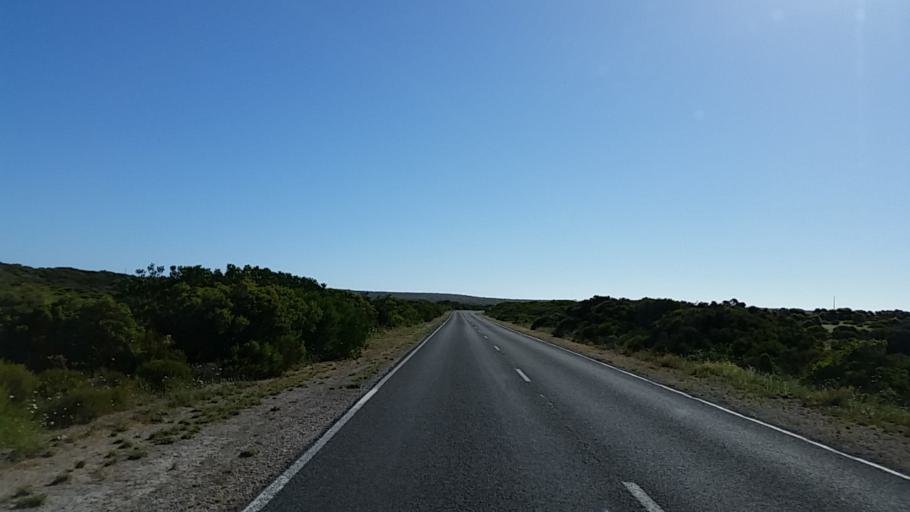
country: AU
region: South Australia
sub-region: Yorke Peninsula
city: Honiton
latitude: -35.2647
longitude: 136.9512
